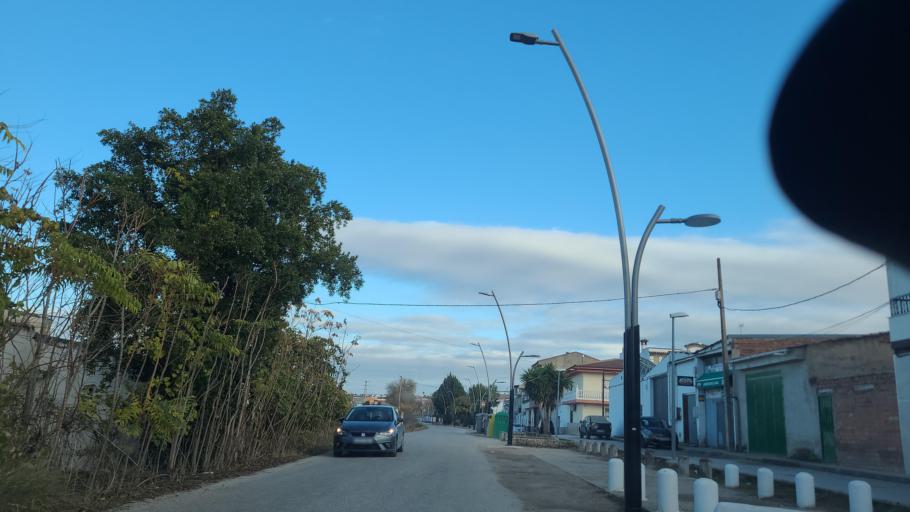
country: ES
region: Andalusia
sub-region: Provincia de Jaen
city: Mengibar
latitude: 37.9732
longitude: -3.8085
